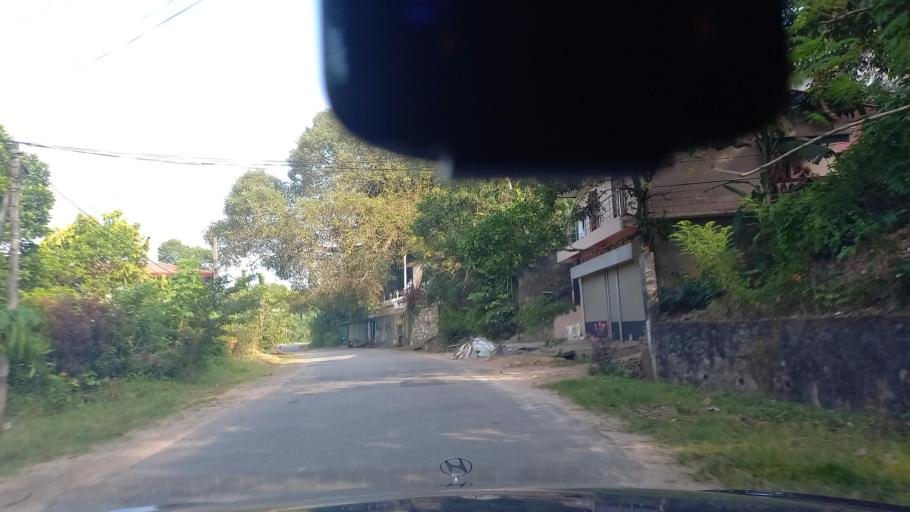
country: LK
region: Central
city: Gampola
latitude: 7.2200
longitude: 80.6066
